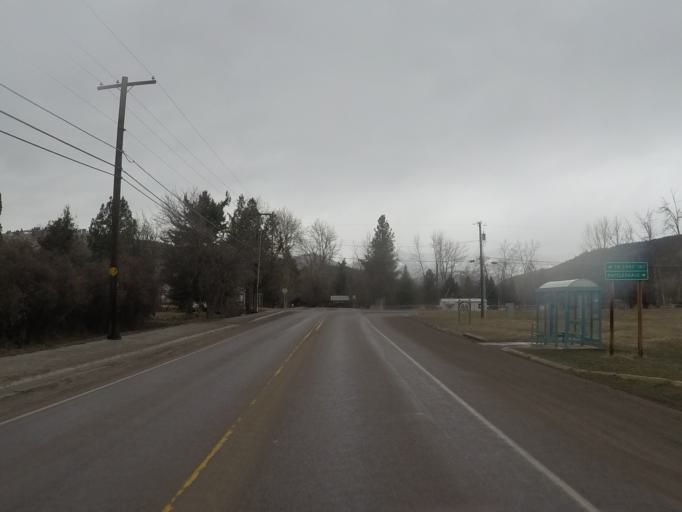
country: US
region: Montana
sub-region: Missoula County
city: East Missoula
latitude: 46.8990
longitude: -113.9656
